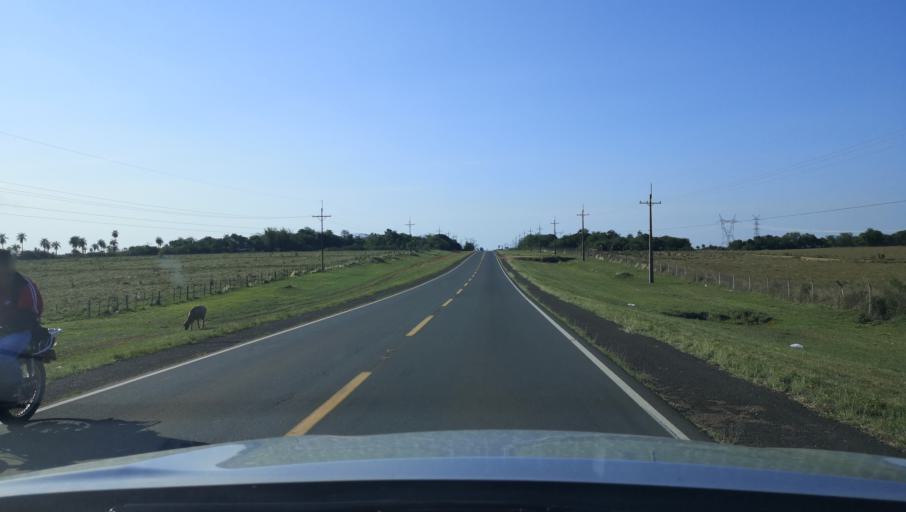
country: PY
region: Misiones
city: Santa Maria
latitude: -26.8033
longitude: -57.0209
